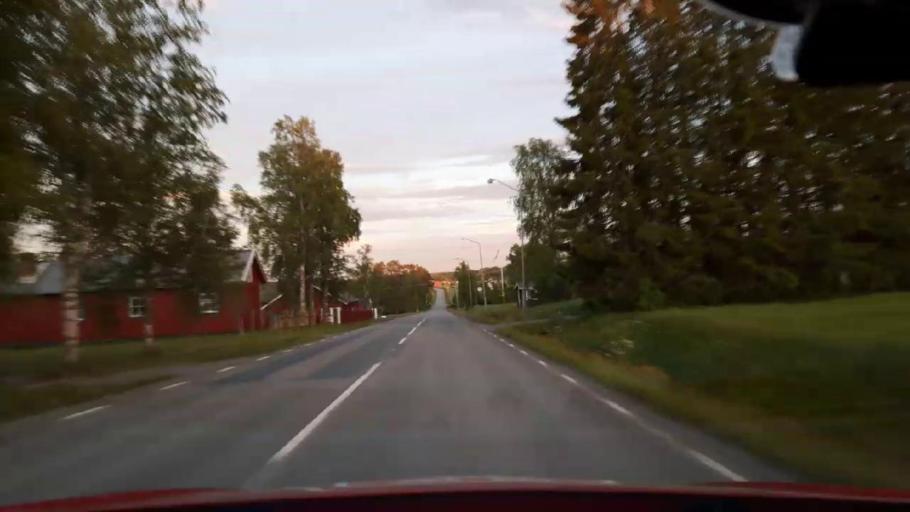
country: SE
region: Jaemtland
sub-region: OEstersunds Kommun
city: Brunflo
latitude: 63.1080
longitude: 14.7347
